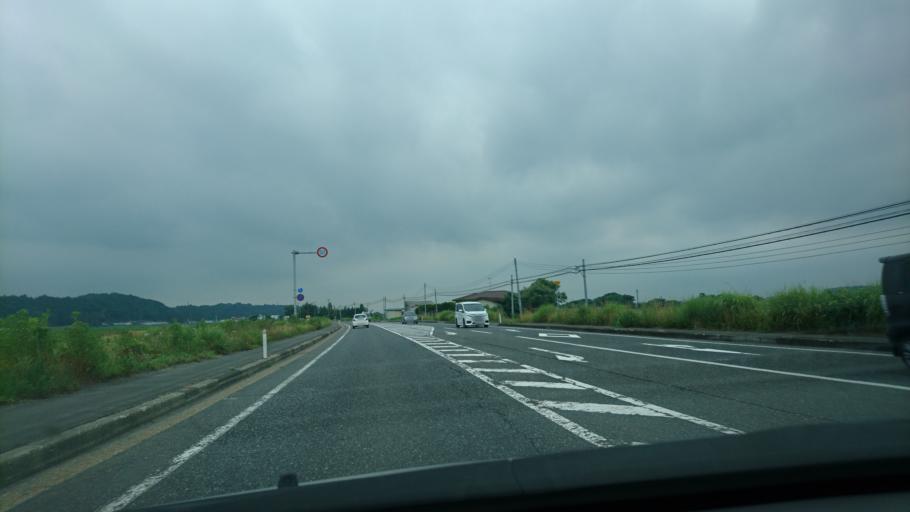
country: JP
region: Miyagi
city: Furukawa
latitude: 38.6632
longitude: 140.8722
